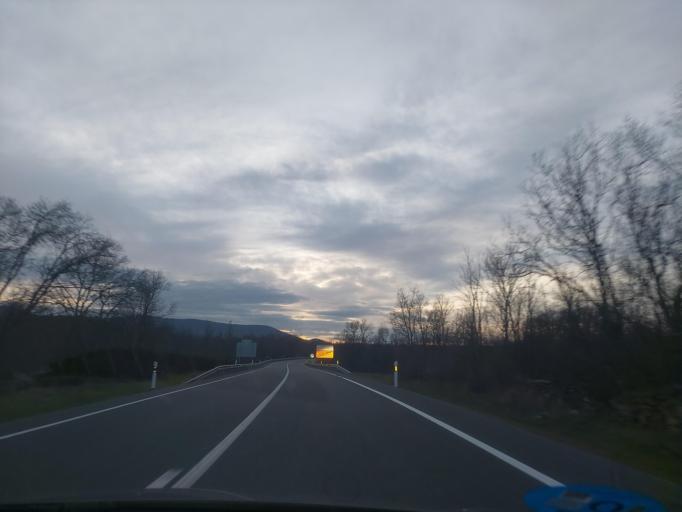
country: ES
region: Castille and Leon
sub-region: Provincia de Segovia
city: Gallegos
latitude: 41.0913
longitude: -3.7818
